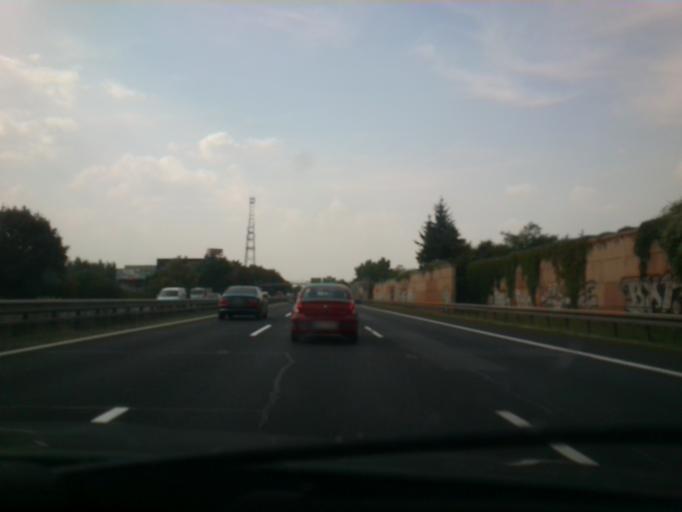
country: CZ
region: Central Bohemia
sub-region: Okres Praha-Vychod
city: Ricany
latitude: 49.9618
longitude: 14.6295
